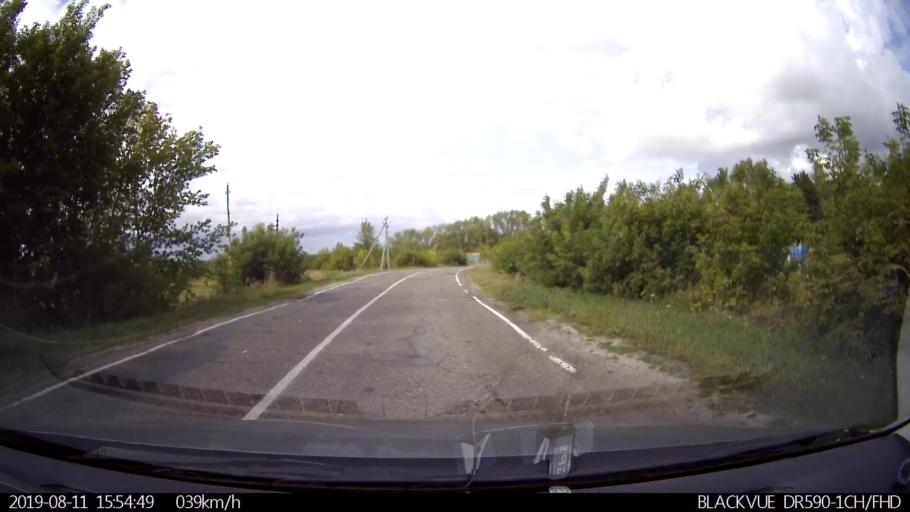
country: RU
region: Ulyanovsk
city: Ignatovka
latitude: 53.9431
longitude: 47.6560
